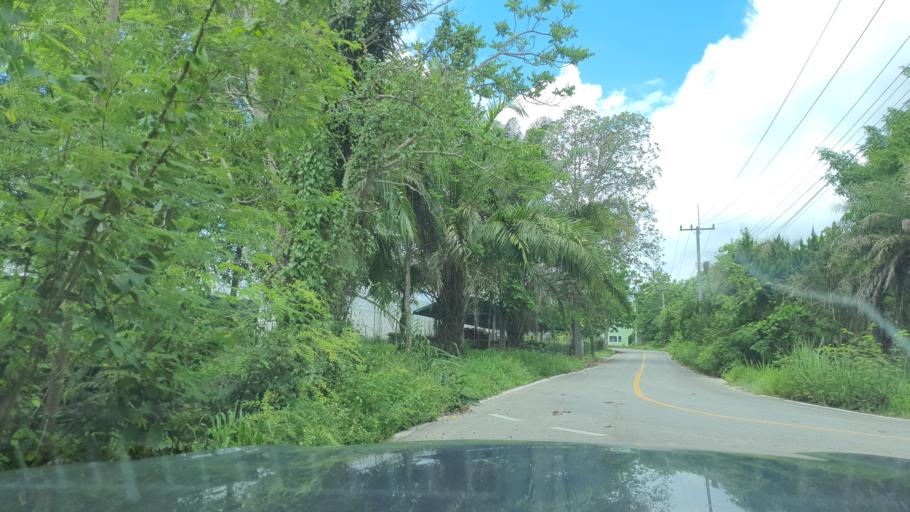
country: TH
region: Chiang Mai
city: San Sai
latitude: 18.9223
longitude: 99.0525
